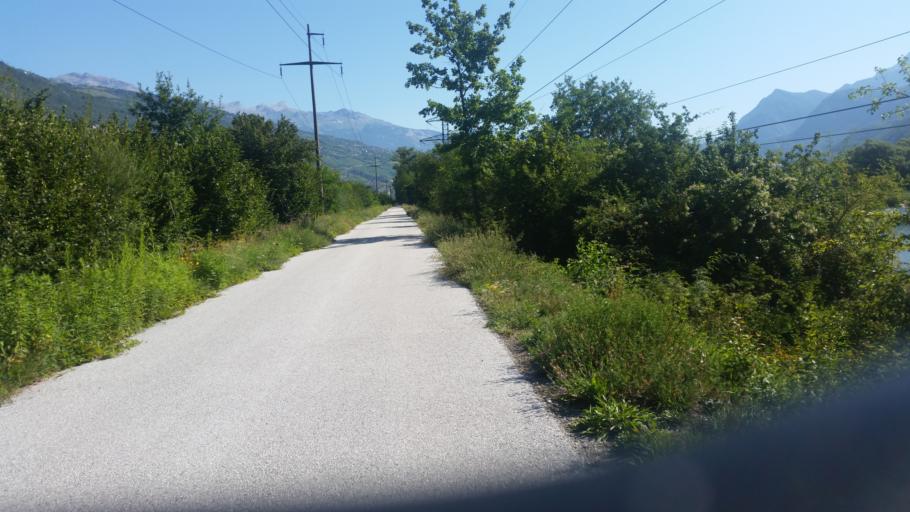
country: CH
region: Valais
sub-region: Sion District
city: Saint-Leonard
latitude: 46.2464
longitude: 7.4304
